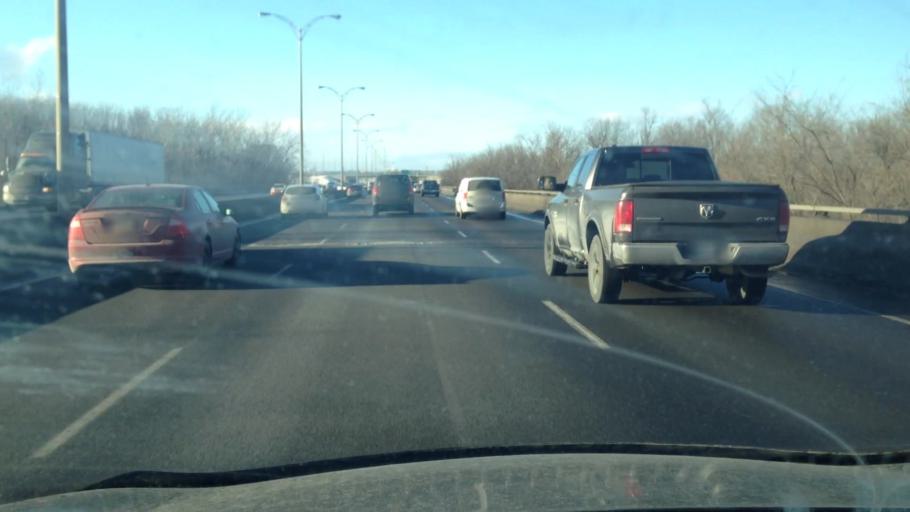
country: CA
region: Quebec
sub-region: Laurentides
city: Boisbriand
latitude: 45.6114
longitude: -73.8142
